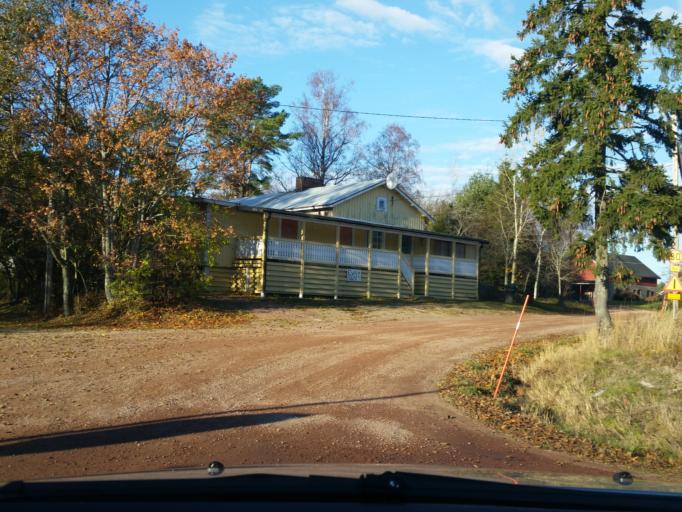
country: AX
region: Alands skaergard
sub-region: Braendoe
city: Braendoe
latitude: 60.4595
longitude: 21.0722
